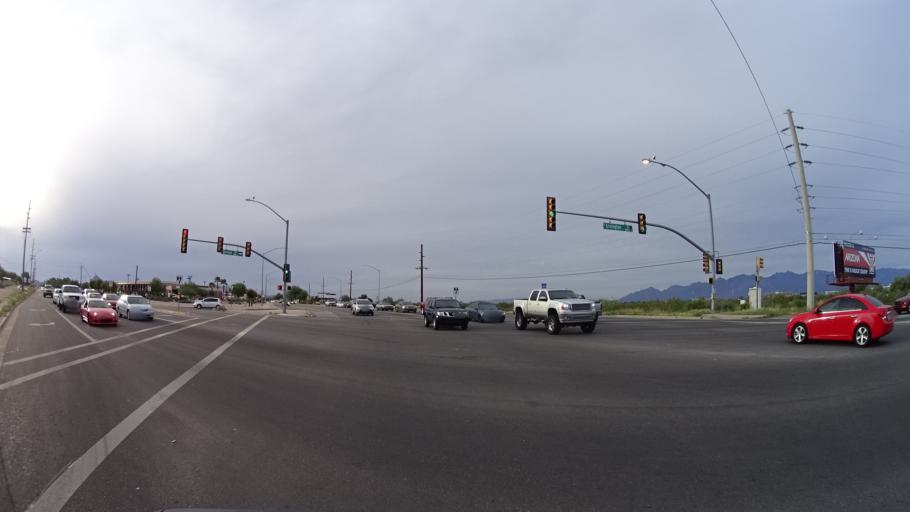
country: US
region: Arizona
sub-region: Pima County
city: South Tucson
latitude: 32.1631
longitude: -110.9356
